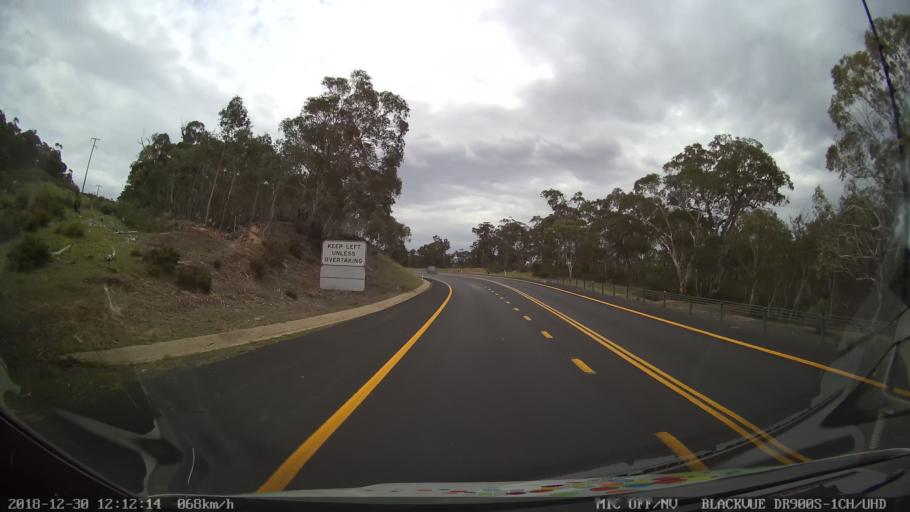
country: AU
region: New South Wales
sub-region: Snowy River
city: Jindabyne
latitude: -36.3590
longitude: 148.5887
